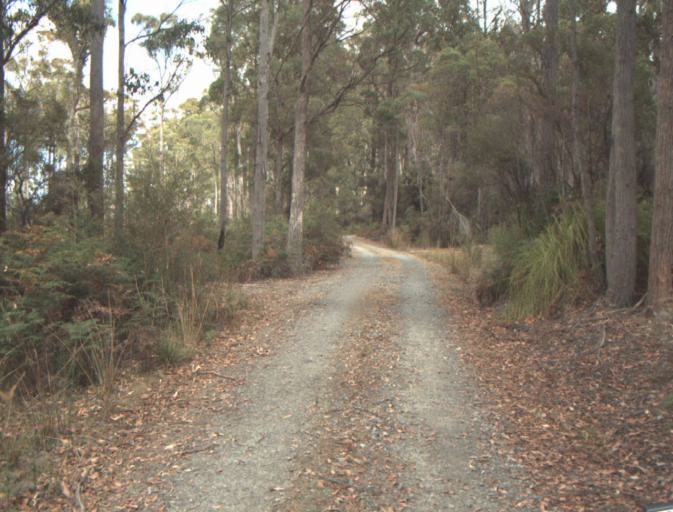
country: AU
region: Tasmania
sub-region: Launceston
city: Mayfield
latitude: -41.1999
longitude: 147.1652
